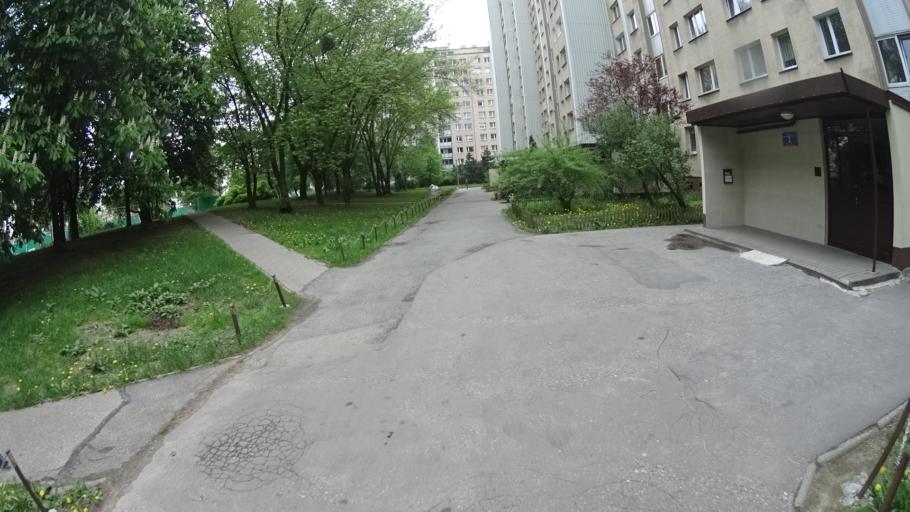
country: PL
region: Masovian Voivodeship
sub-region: Warszawa
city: Bemowo
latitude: 52.2378
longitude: 20.9095
